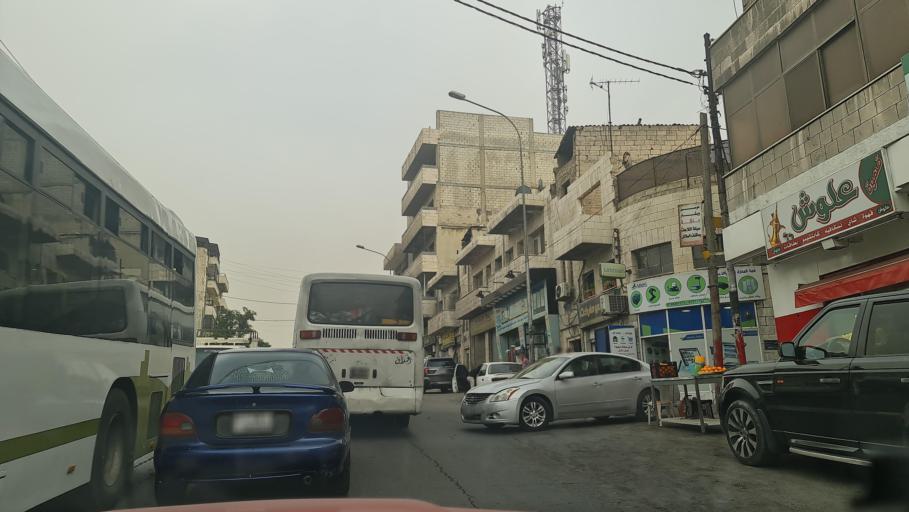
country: JO
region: Amman
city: Amman
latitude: 31.9341
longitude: 35.9327
